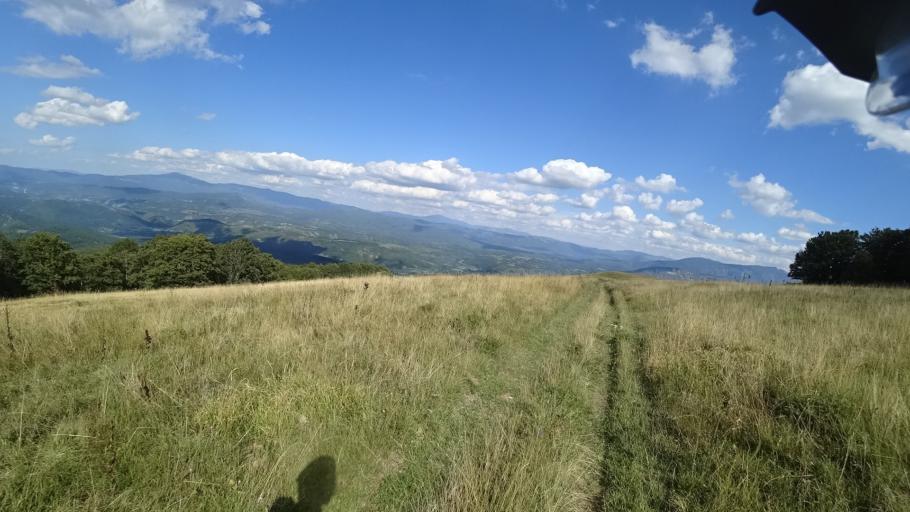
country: HR
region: Zadarska
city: Gracac
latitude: 44.3688
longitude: 16.0750
